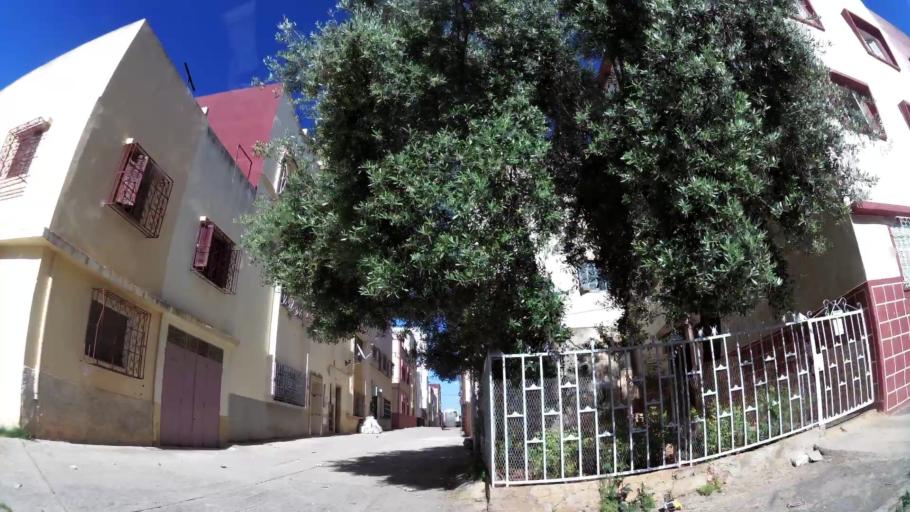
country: MA
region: Meknes-Tafilalet
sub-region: Meknes
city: Meknes
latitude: 33.8973
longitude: -5.5017
